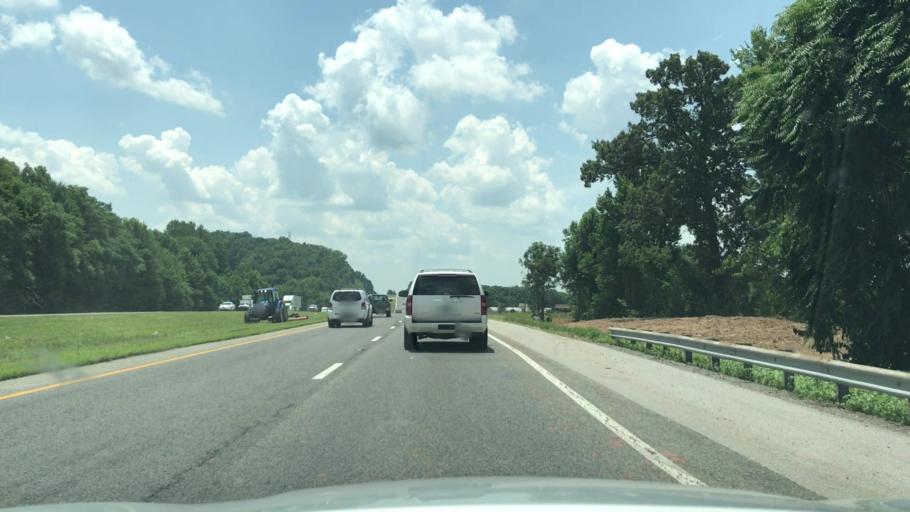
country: US
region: Tennessee
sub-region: Putnam County
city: Cookeville
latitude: 36.1460
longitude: -85.4771
